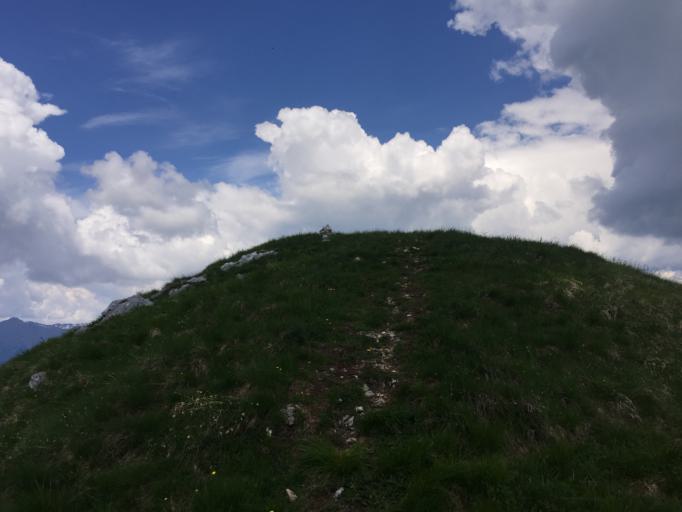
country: IT
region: Friuli Venezia Giulia
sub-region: Provincia di Udine
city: Sutrio
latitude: 46.4775
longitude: 12.9705
